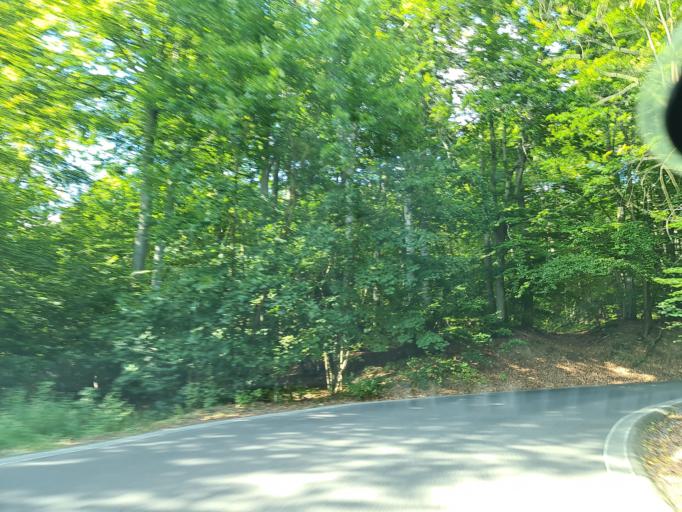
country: CZ
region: Ustecky
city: Mezibori
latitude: 50.6122
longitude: 13.5734
